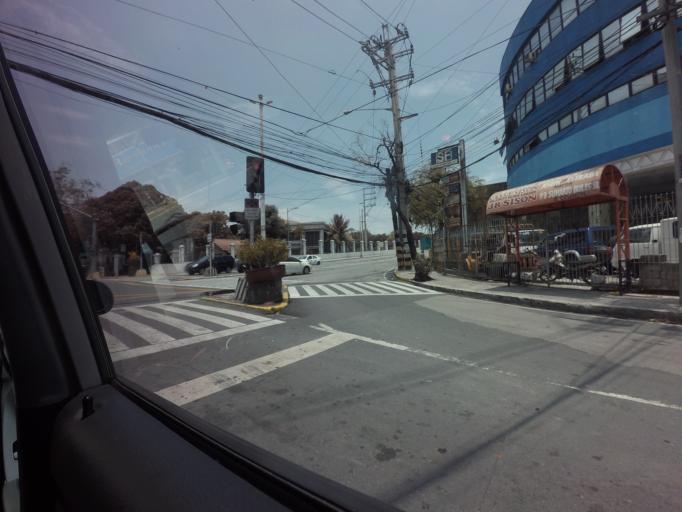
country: PH
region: Metro Manila
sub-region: City of Manila
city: Quiapo
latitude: 14.5925
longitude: 120.9869
